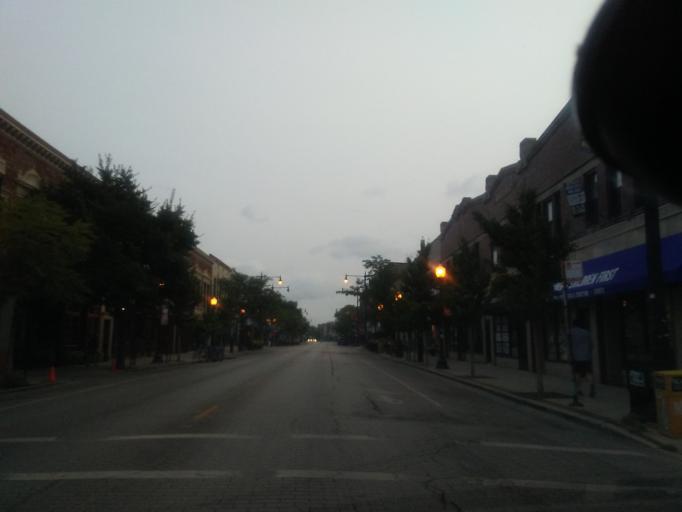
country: US
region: Illinois
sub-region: Cook County
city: Lincolnwood
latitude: 41.9771
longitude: -87.6684
